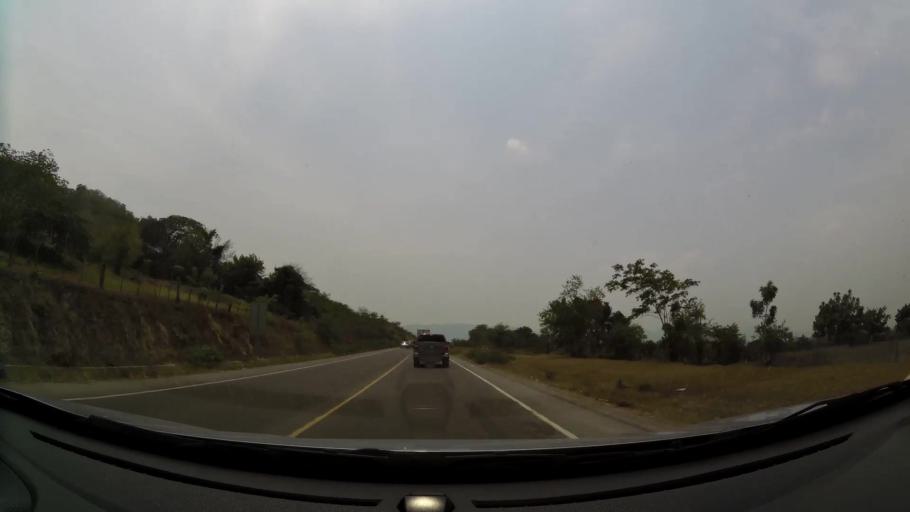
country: HN
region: Cortes
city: El Plan
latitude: 15.2639
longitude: -87.9635
